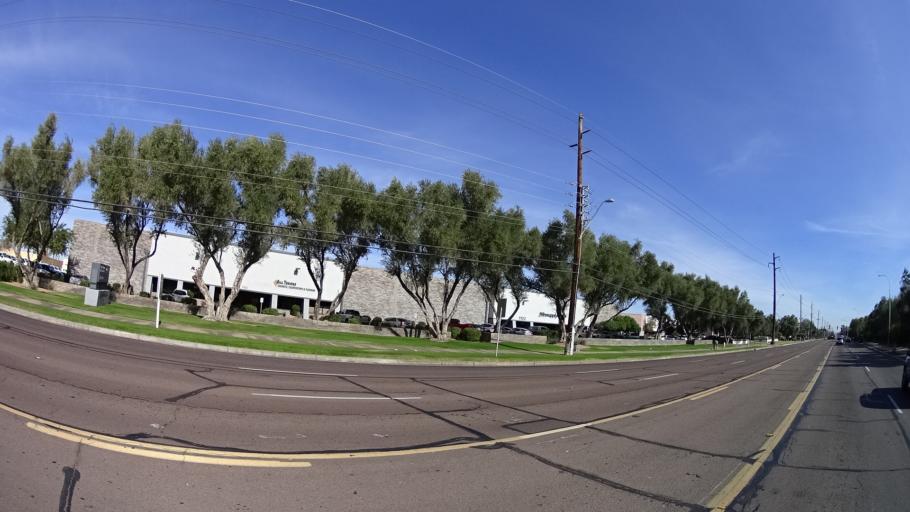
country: US
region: Arizona
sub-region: Maricopa County
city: Guadalupe
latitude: 33.3928
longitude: -111.9548
